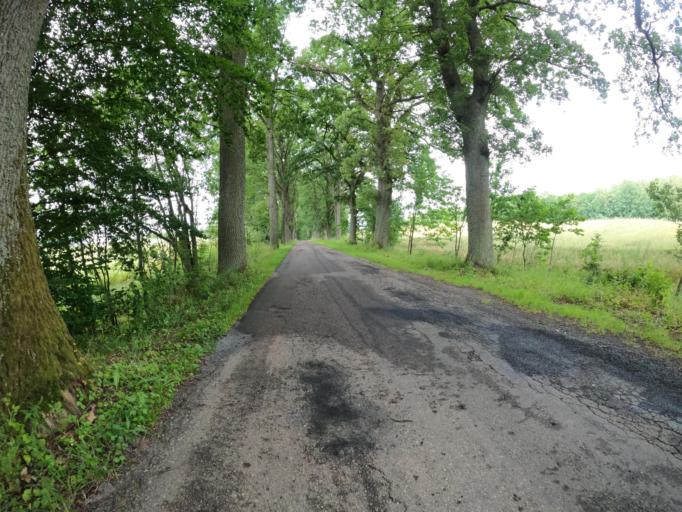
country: PL
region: West Pomeranian Voivodeship
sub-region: Powiat szczecinecki
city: Grzmiaca
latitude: 53.9281
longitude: 16.4801
